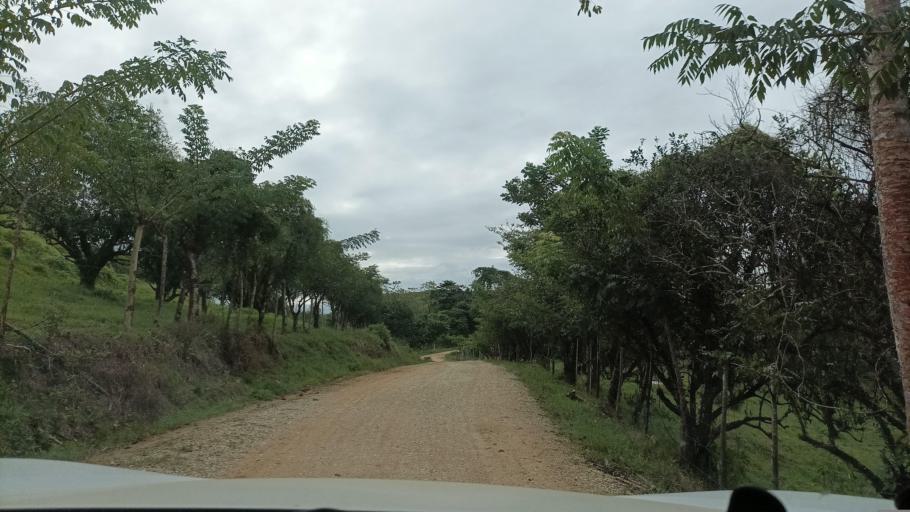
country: MX
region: Veracruz
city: Hidalgotitlan
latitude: 17.6024
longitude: -94.4237
